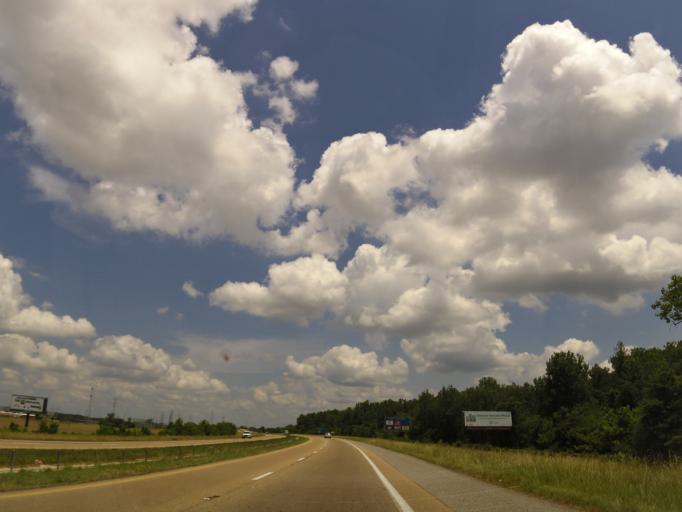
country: US
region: Mississippi
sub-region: Lee County
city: Tupelo
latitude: 34.2464
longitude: -88.6946
